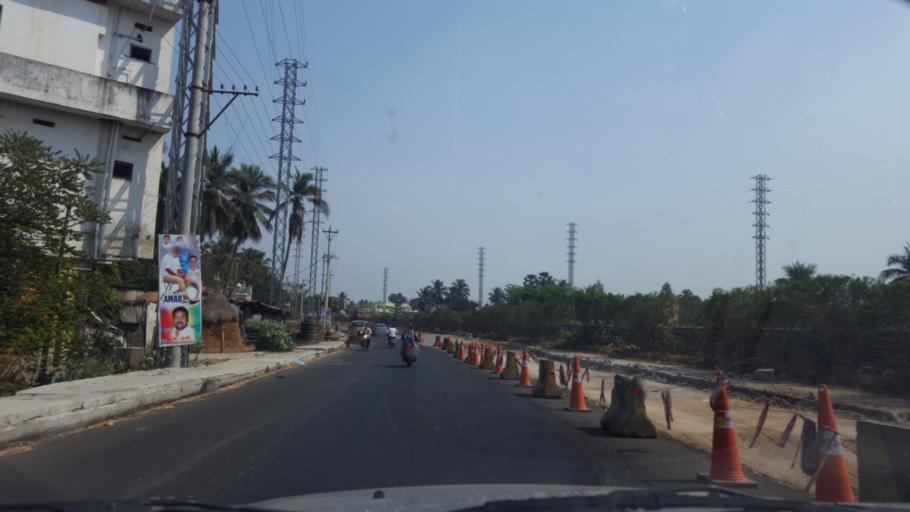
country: IN
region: Andhra Pradesh
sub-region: Vishakhapatnam
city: Anakapalle
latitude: 17.6756
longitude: 82.9970
